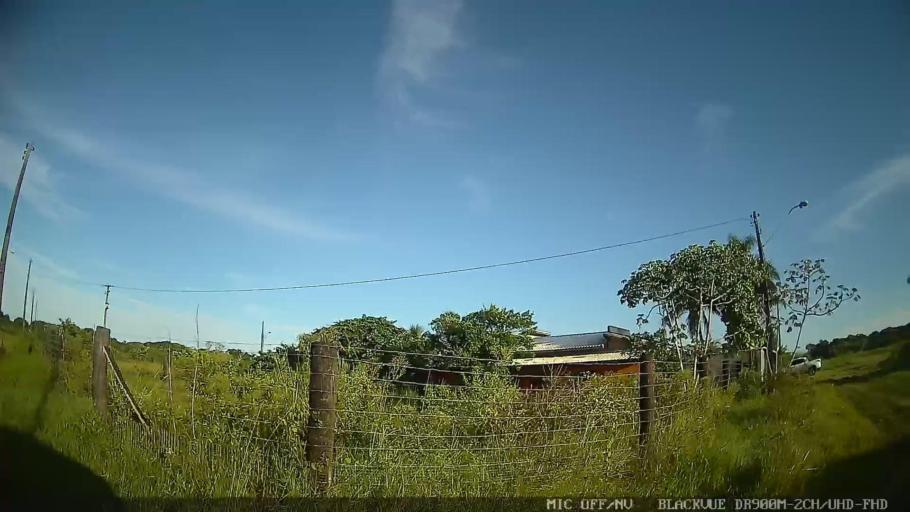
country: BR
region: Sao Paulo
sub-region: Iguape
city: Iguape
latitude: -24.7529
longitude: -47.5686
